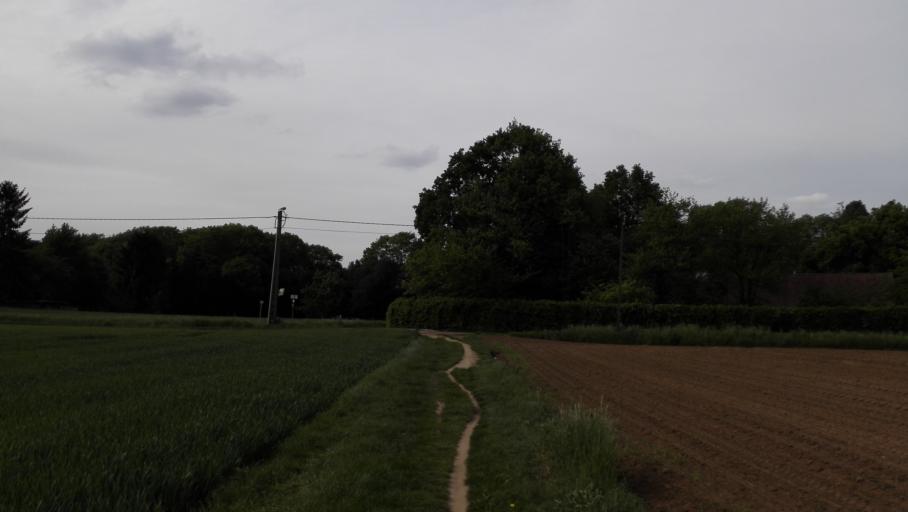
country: BE
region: Flanders
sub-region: Provincie Vlaams-Brabant
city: Holsbeek
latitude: 50.9113
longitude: 4.7570
